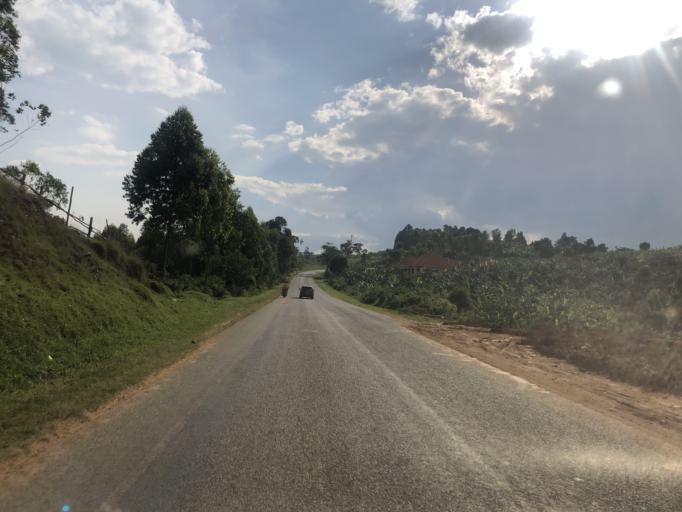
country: UG
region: Western Region
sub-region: Bushenyi District
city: Bushenyi
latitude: -0.5431
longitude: 30.2088
